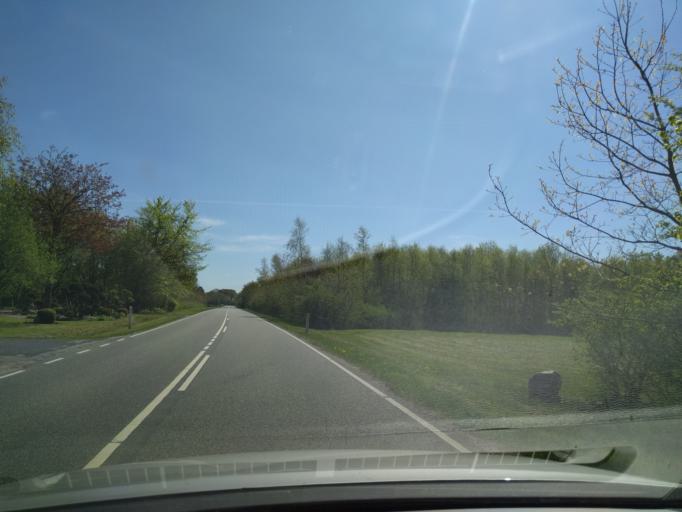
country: DK
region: Central Jutland
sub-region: Ringkobing-Skjern Kommune
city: Tarm
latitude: 55.8867
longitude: 8.5171
